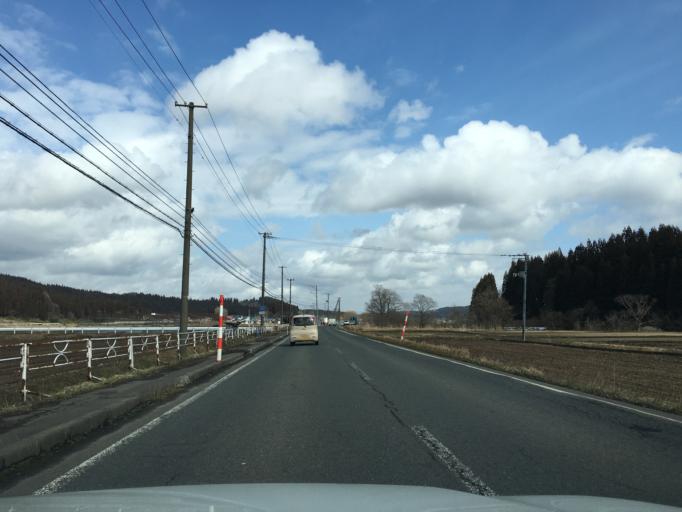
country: JP
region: Akita
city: Takanosu
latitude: 40.0370
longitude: 140.2772
